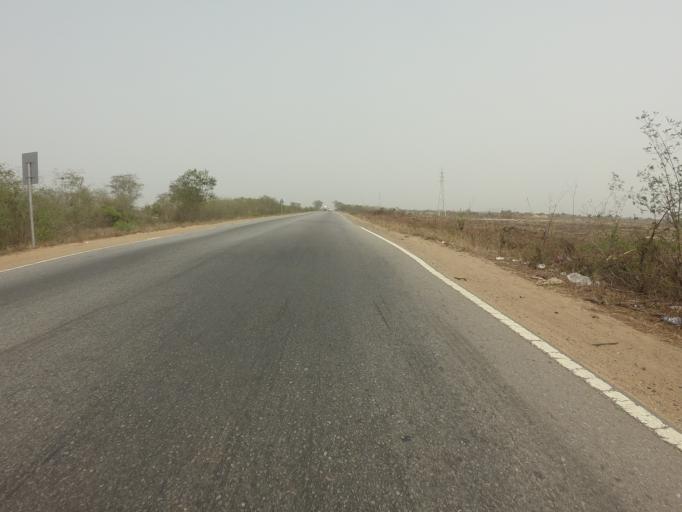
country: GH
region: Greater Accra
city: Tema
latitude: 5.7966
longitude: 0.1294
